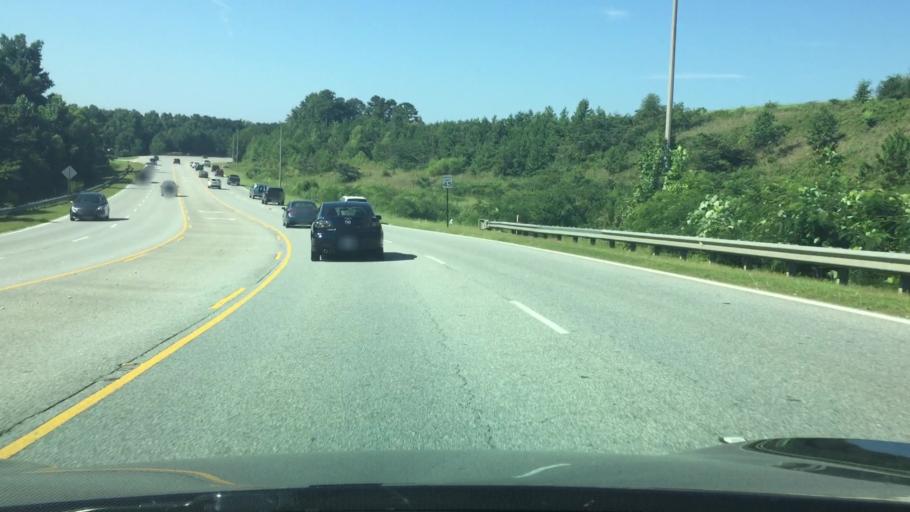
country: US
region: Alabama
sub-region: Lee County
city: Auburn
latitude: 32.6078
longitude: -85.4325
